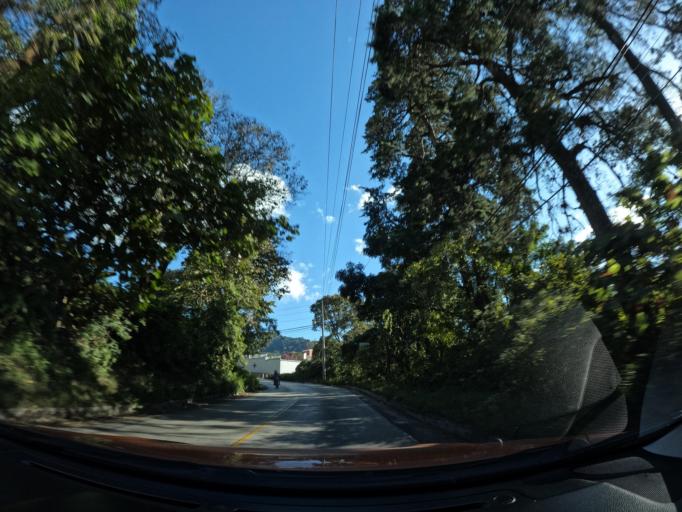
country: GT
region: Sacatepequez
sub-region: Municipio de Santa Maria de Jesus
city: Santa Maria de Jesus
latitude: 14.5206
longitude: -90.7236
